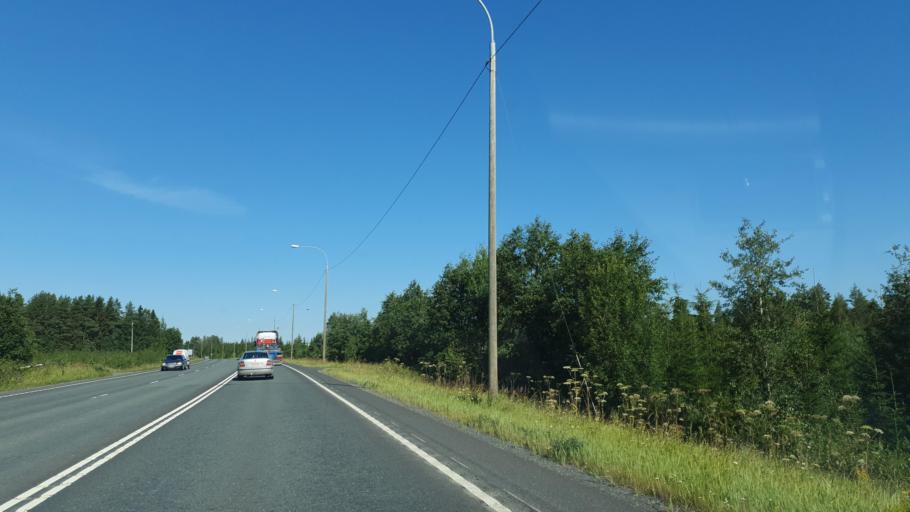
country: FI
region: Northern Savo
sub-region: Ylae-Savo
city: Lapinlahti
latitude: 63.2346
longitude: 27.5021
